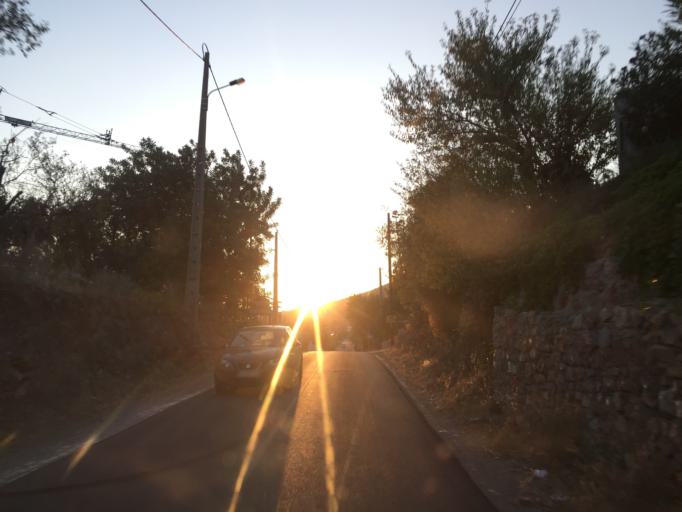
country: PT
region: Faro
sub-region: Faro
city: Santa Barbara de Nexe
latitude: 37.1048
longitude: -7.9703
